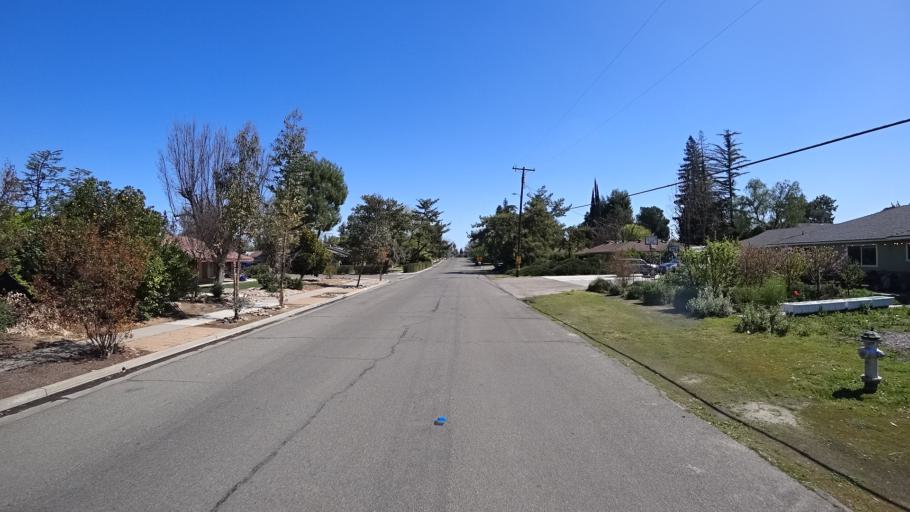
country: US
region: California
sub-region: Fresno County
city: Fresno
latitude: 36.8265
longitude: -119.8151
